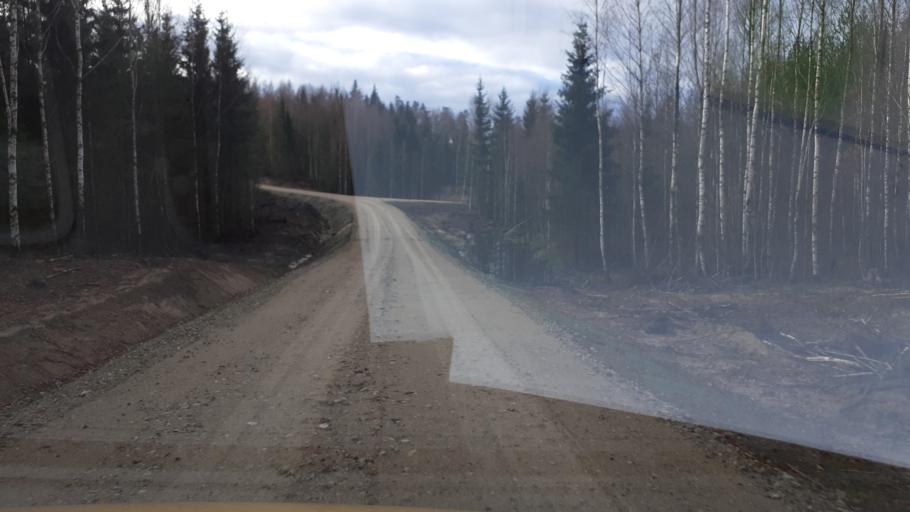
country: LV
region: Skrunda
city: Skrunda
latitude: 56.7901
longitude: 21.8359
